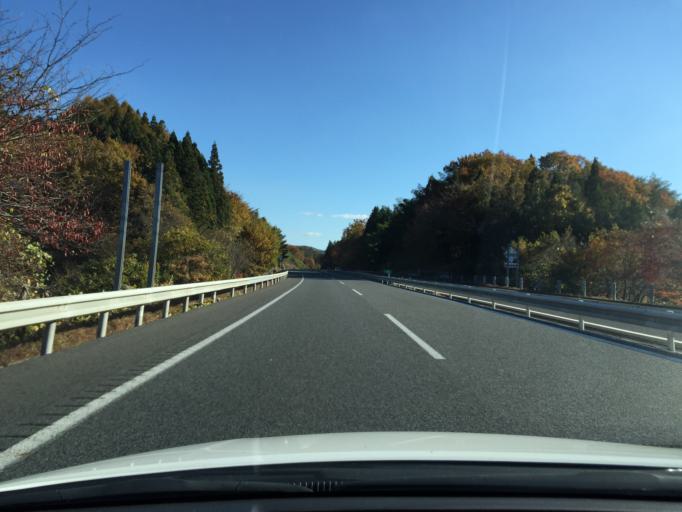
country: JP
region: Fukushima
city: Funehikimachi-funehiki
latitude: 37.3733
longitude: 140.6012
